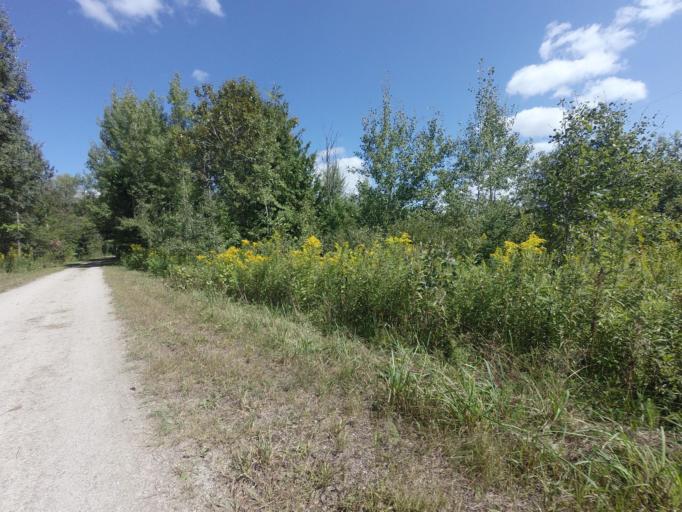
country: CA
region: Ontario
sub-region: Wellington County
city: Guelph
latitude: 43.7638
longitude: -80.3254
